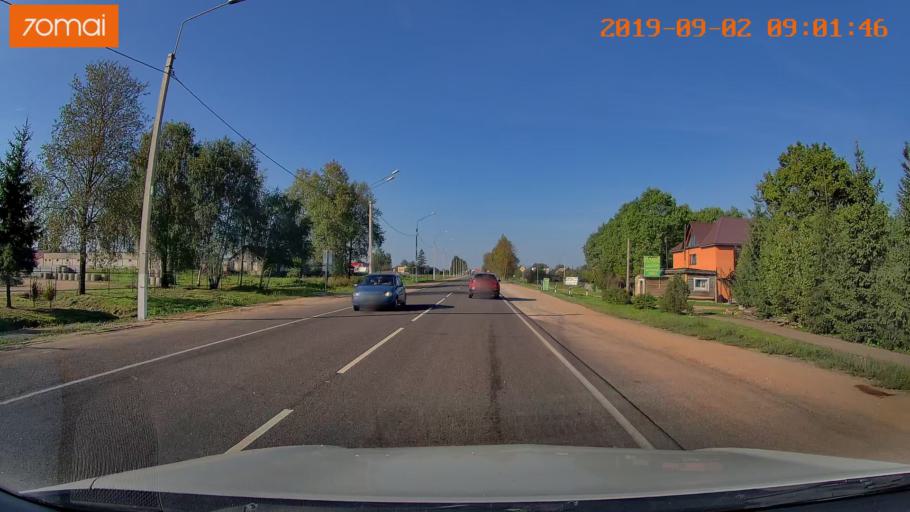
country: RU
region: Kaluga
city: Myatlevo
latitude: 54.9041
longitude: 35.6819
